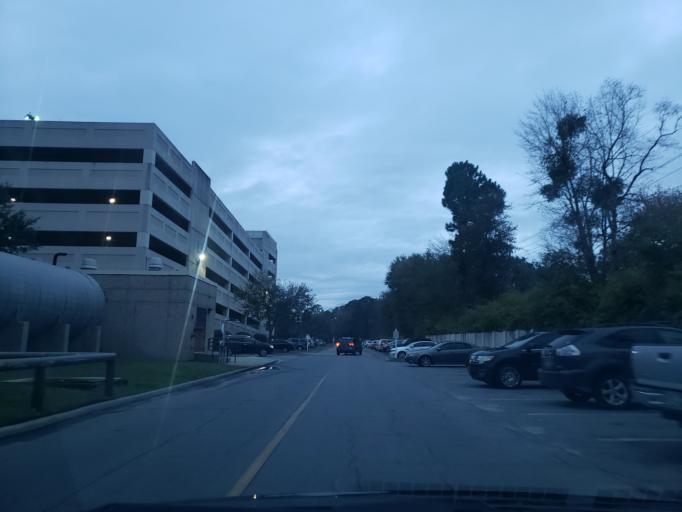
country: US
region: Georgia
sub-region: Chatham County
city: Thunderbolt
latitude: 32.0296
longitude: -81.0987
